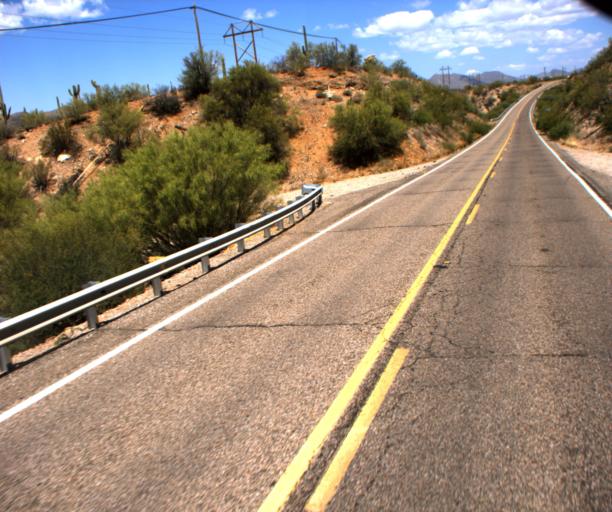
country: US
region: Arizona
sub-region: Pinal County
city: Kearny
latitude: 33.0731
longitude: -110.9194
